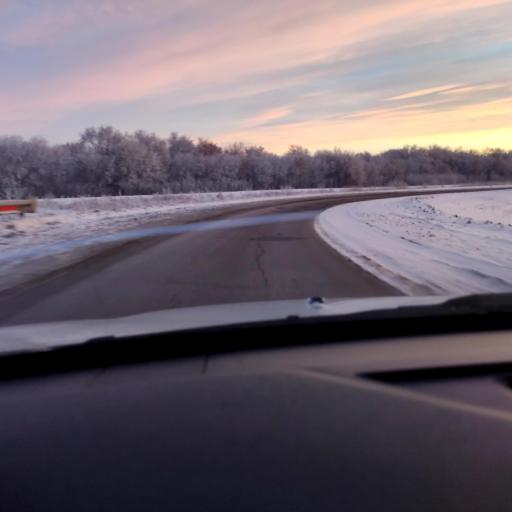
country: RU
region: Samara
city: Smyshlyayevka
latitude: 53.2629
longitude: 50.4739
